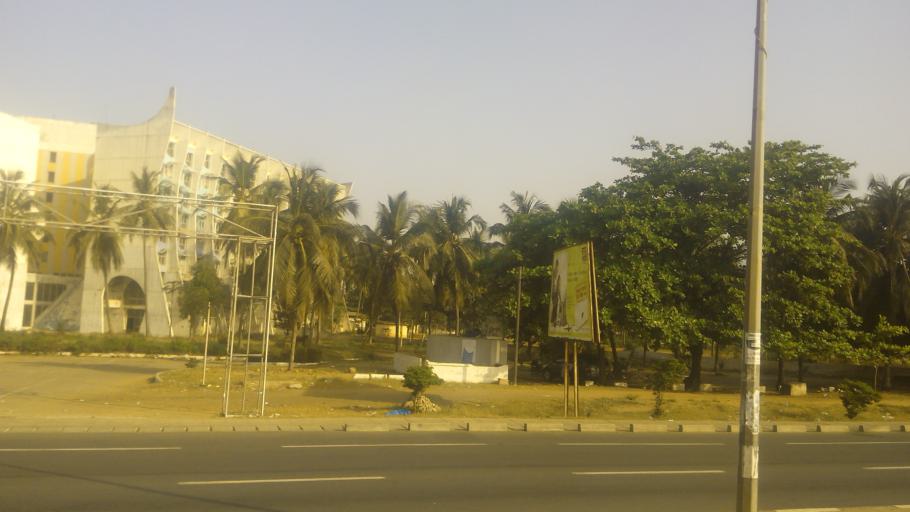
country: TG
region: Maritime
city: Lome
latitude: 6.1309
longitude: 1.2474
